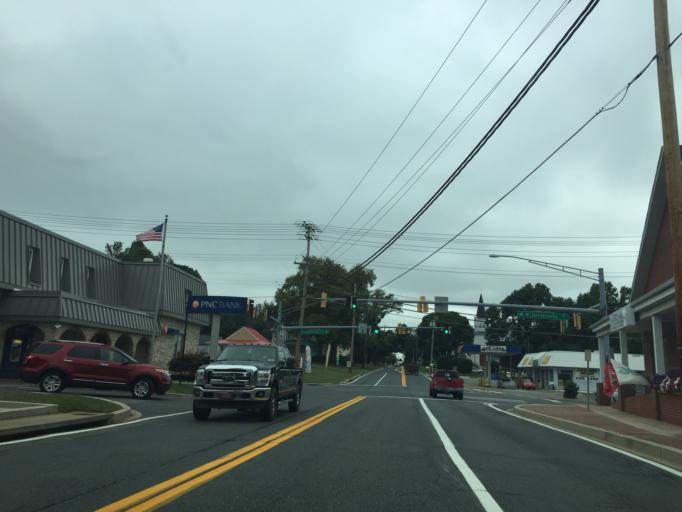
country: US
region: Maryland
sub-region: Harford County
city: Bel Air North
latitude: 39.5846
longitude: -76.3877
